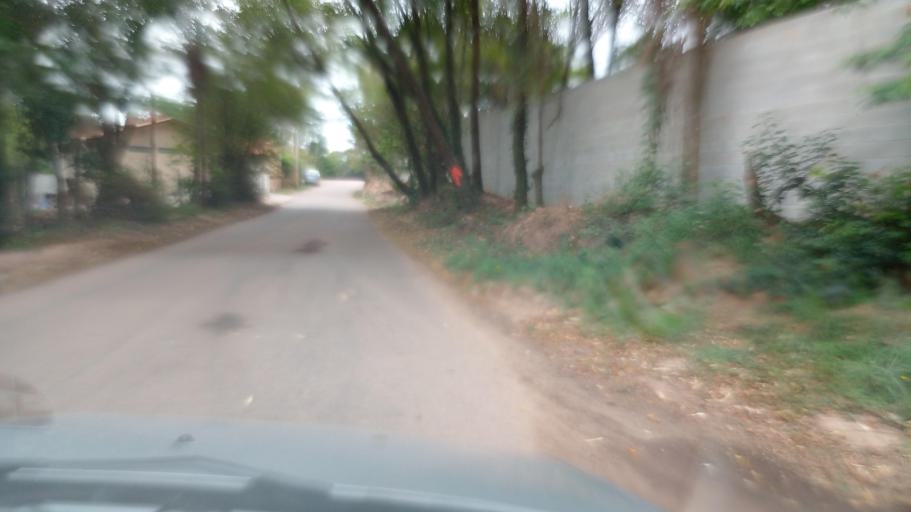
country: BR
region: Sao Paulo
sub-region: Jundiai
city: Jundiai
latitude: -23.1355
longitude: -46.9089
